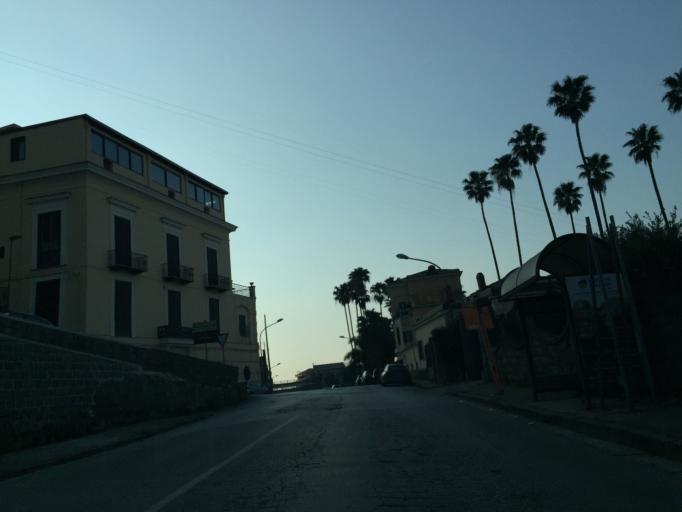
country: IT
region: Campania
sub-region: Provincia di Napoli
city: Castellammare di Stabia
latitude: 40.6869
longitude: 14.4840
